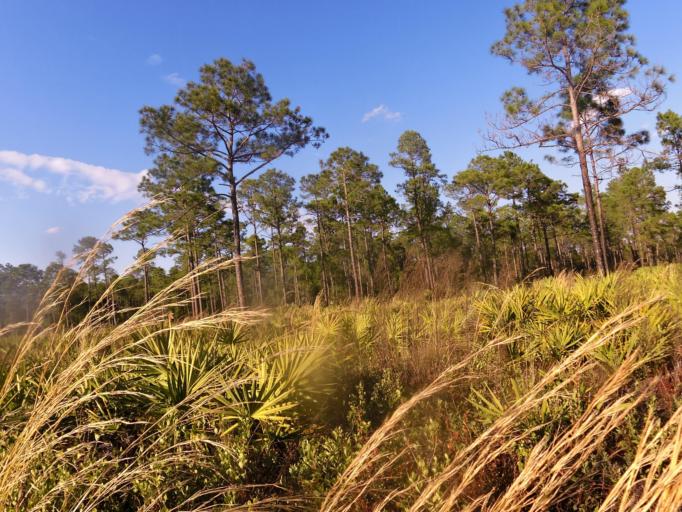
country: US
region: Florida
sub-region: Duval County
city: Atlantic Beach
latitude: 30.4751
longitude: -81.4949
